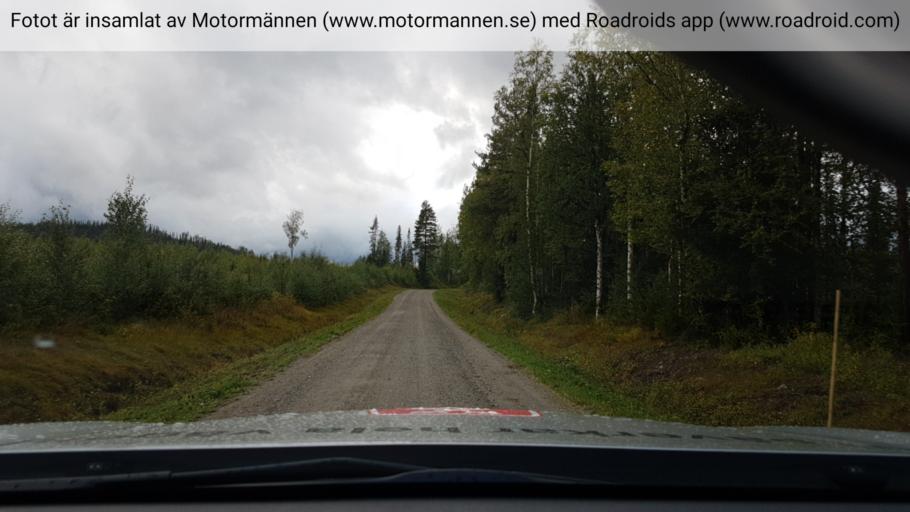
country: SE
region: Vaesterbotten
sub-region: Asele Kommun
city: Asele
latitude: 64.1490
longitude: 16.9464
